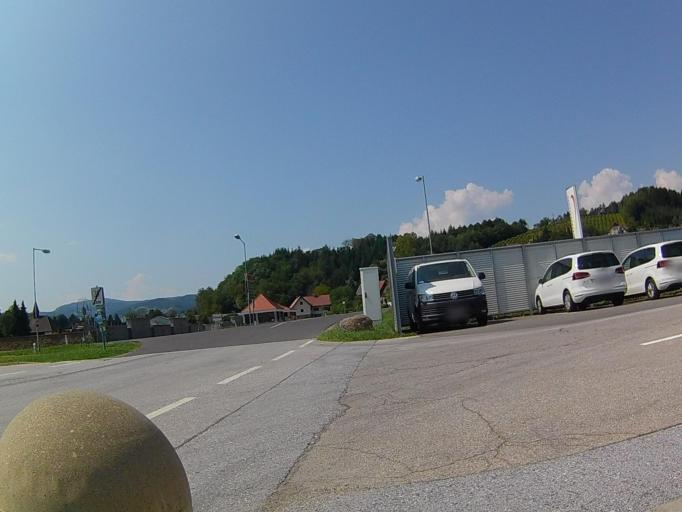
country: AT
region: Styria
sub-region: Politischer Bezirk Deutschlandsberg
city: Eibiswald
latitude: 46.6915
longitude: 15.2483
